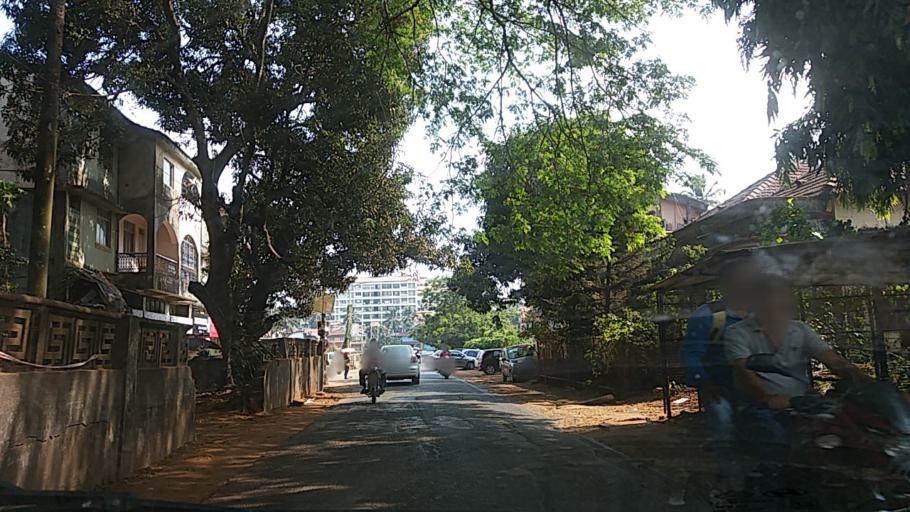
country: IN
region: Goa
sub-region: North Goa
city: Panaji
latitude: 15.4796
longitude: 73.8121
